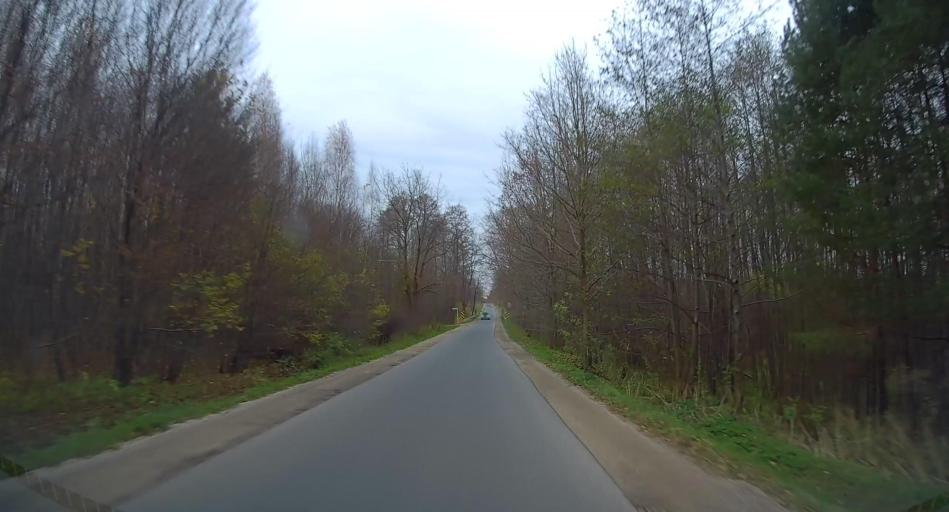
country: PL
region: Lodz Voivodeship
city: Zabia Wola
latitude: 51.9995
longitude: 20.6584
